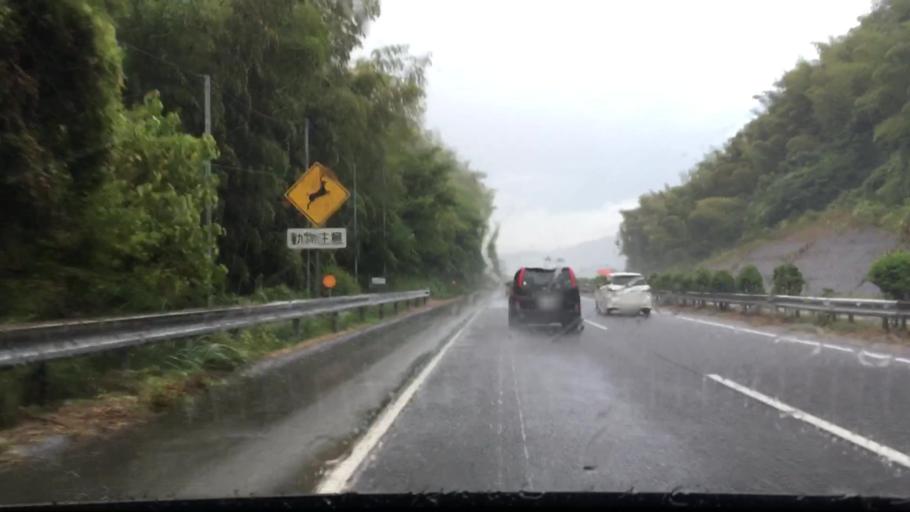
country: JP
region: Fukuoka
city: Kitakyushu
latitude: 33.8085
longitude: 130.8238
